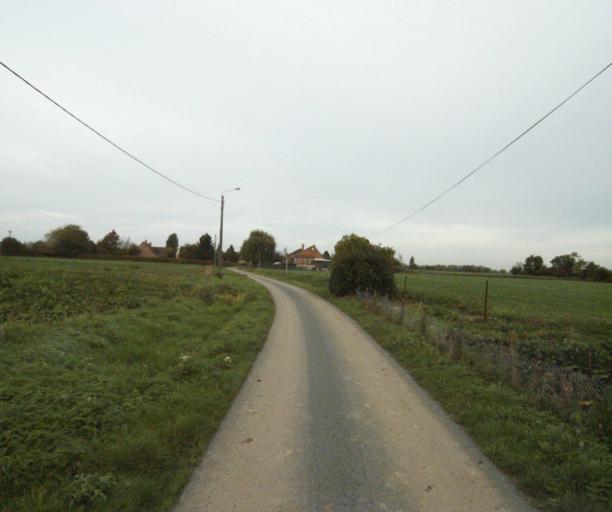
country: FR
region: Nord-Pas-de-Calais
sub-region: Departement du Nord
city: Aubers
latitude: 50.5938
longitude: 2.8369
